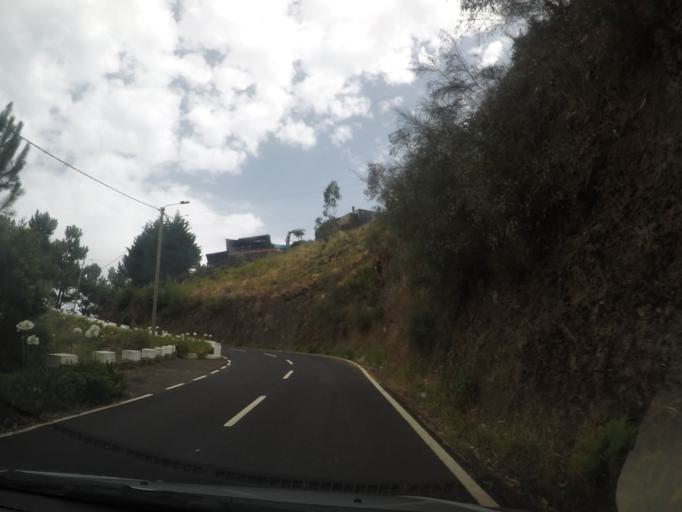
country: PT
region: Madeira
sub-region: Santa Cruz
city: Camacha
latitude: 32.6906
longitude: -16.8431
